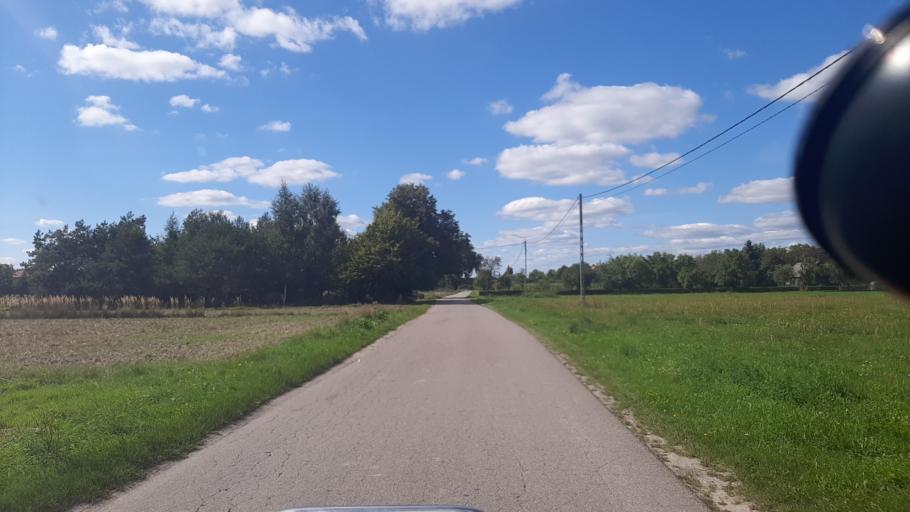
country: PL
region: Lublin Voivodeship
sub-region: Powiat lubelski
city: Garbow
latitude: 51.4064
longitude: 22.4016
